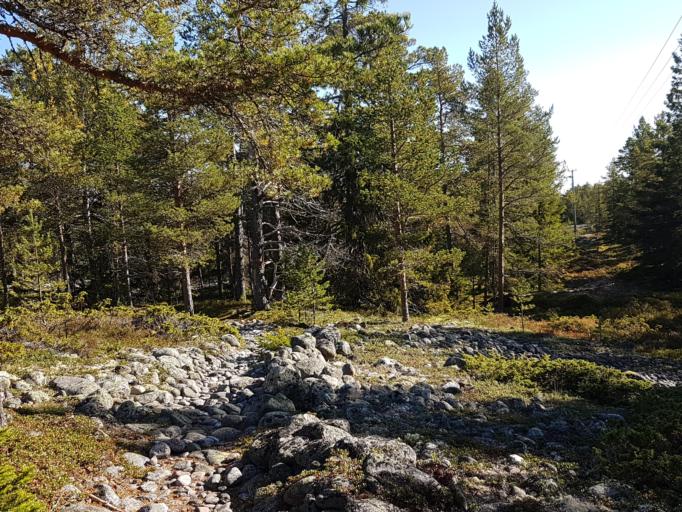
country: SE
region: Vaesterbotten
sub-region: Skelleftea Kommun
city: Skelleftehamn
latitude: 64.4784
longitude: 21.5765
